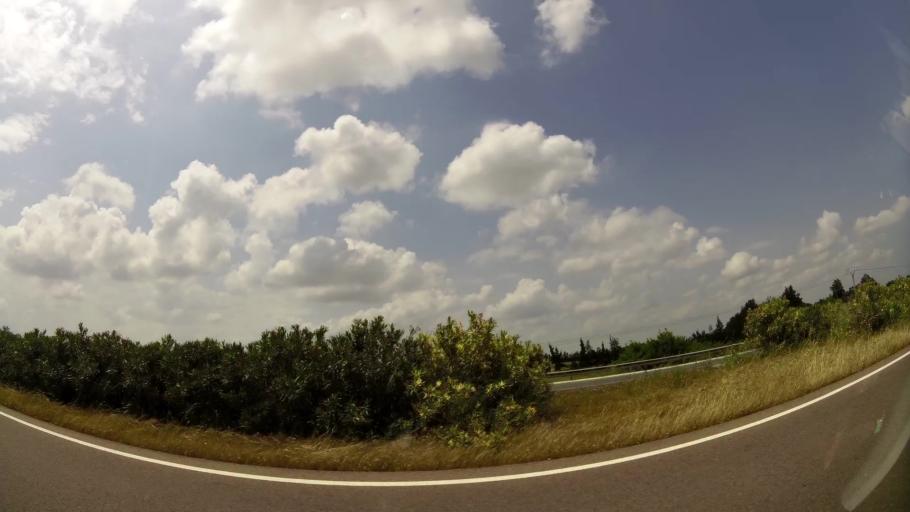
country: MA
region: Rabat-Sale-Zemmour-Zaer
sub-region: Khemisset
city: Tiflet
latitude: 33.9786
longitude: -6.5192
